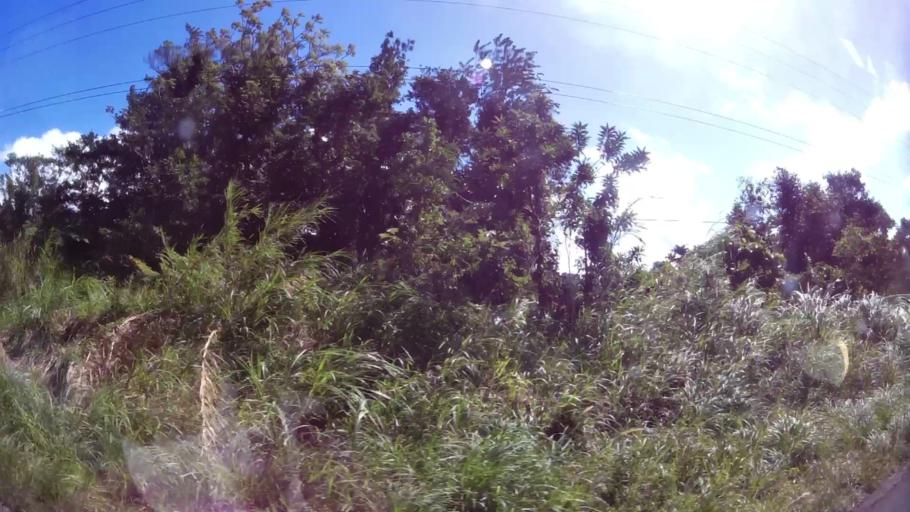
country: DM
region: Saint Paul
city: Pont Casse
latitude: 15.3480
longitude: -61.3626
